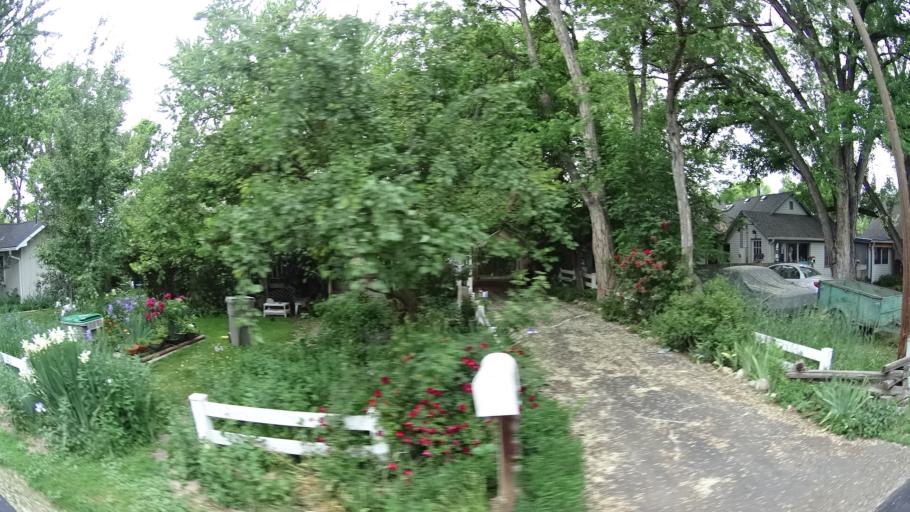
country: US
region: Idaho
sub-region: Ada County
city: Boise
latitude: 43.5799
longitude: -116.2037
